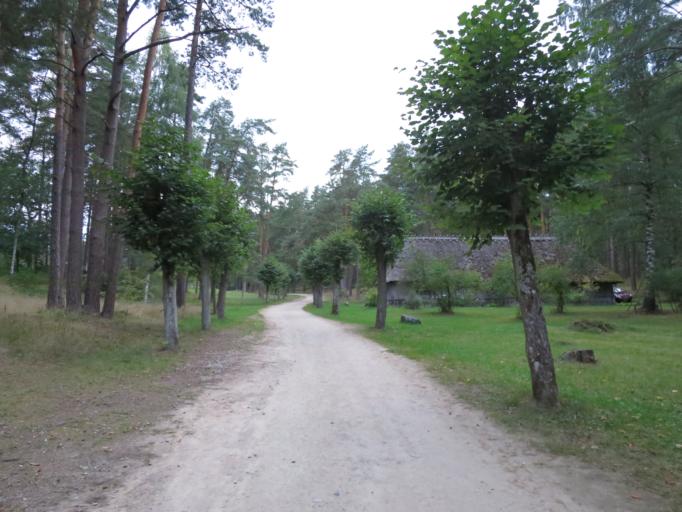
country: LV
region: Riga
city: Bergi
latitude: 56.9925
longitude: 24.2759
